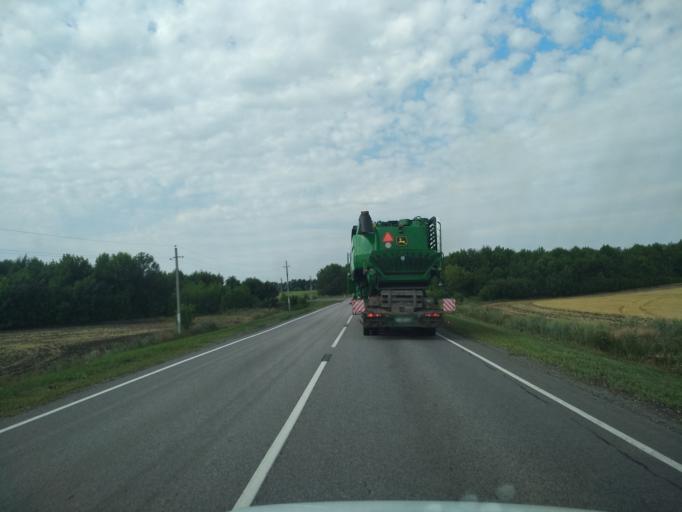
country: RU
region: Voronezj
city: Pereleshinskiy
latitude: 51.8789
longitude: 40.4160
